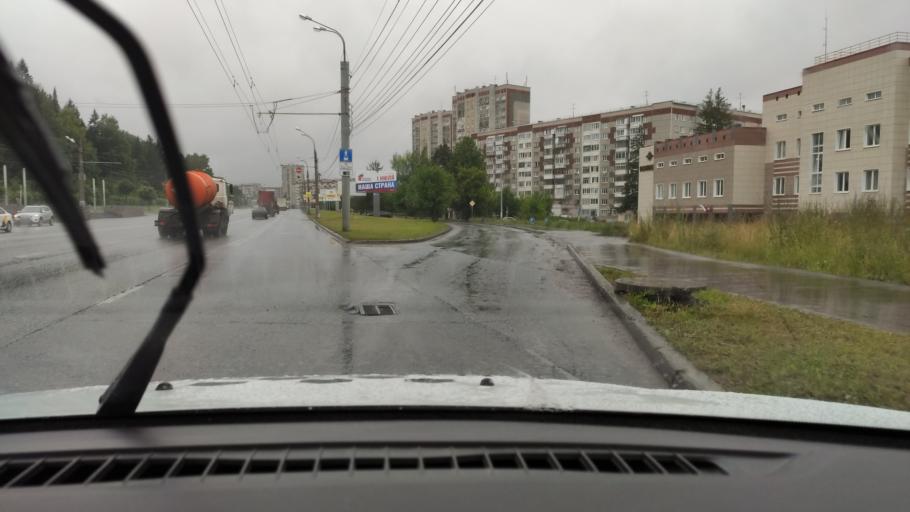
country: RU
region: Udmurtiya
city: Izhevsk
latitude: 56.8820
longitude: 53.2253
